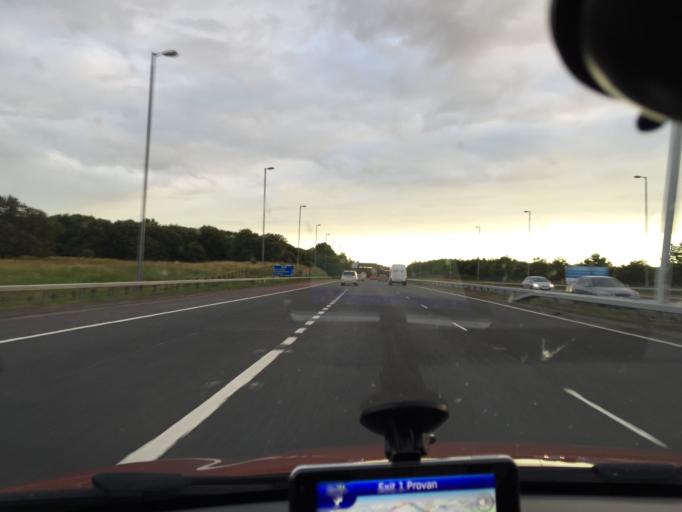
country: GB
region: Scotland
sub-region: North Lanarkshire
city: Stepps
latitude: 55.8868
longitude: -4.1831
